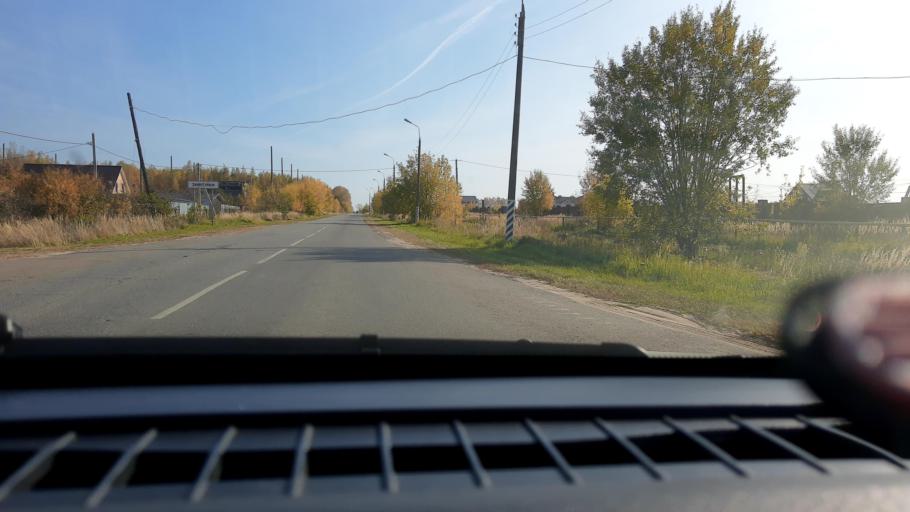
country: RU
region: Nizjnij Novgorod
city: Kstovo
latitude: 56.1557
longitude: 44.2716
